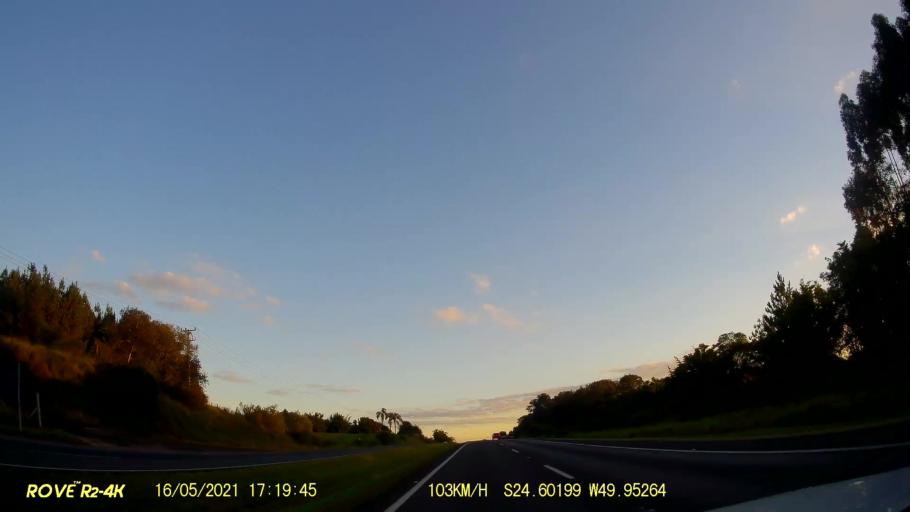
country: BR
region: Parana
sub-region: Pirai Do Sul
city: Pirai do Sul
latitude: -24.6021
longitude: -49.9530
